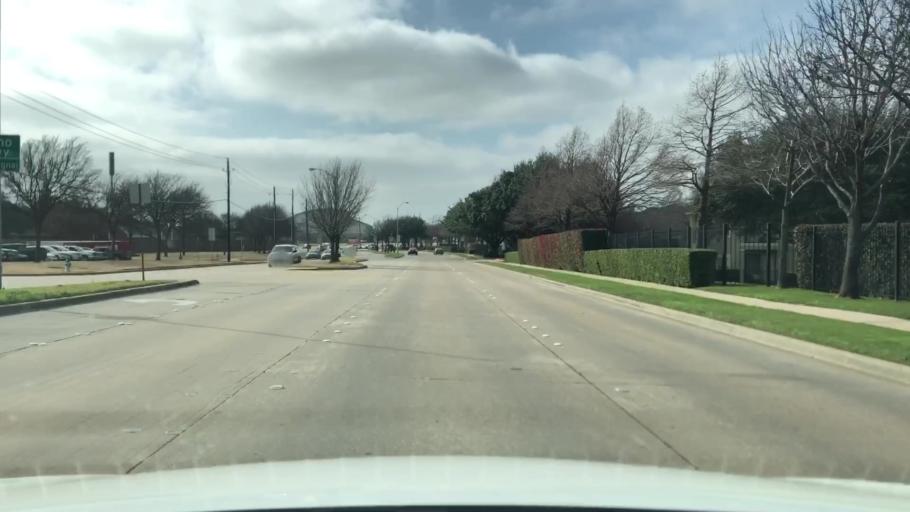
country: US
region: Texas
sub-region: Dallas County
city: Addison
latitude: 33.0330
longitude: -96.8400
